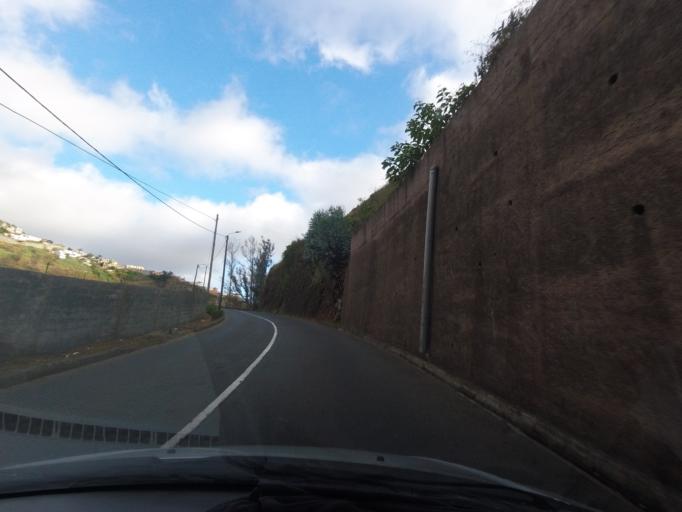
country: PT
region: Madeira
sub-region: Funchal
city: Nossa Senhora do Monte
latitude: 32.6744
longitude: -16.9186
